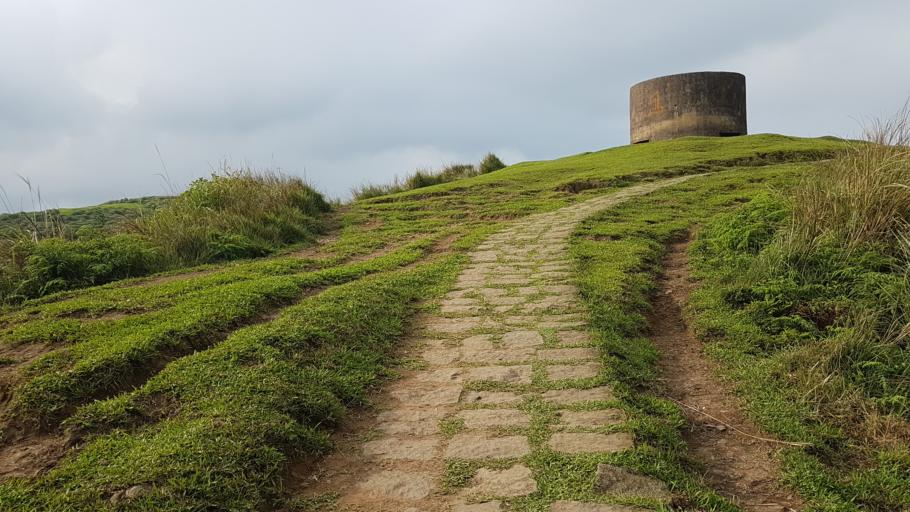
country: TW
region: Taipei
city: Taipei
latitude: 25.1640
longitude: 121.5778
